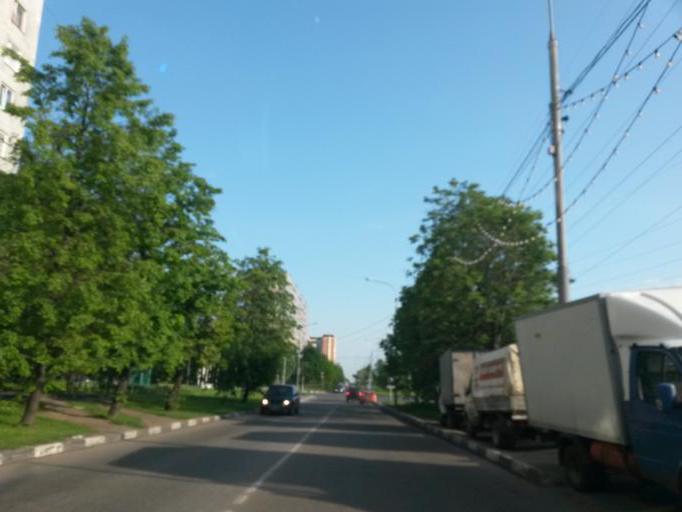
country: RU
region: Moskovskaya
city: Biryulevo Zapadnoye
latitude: 55.5886
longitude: 37.6391
